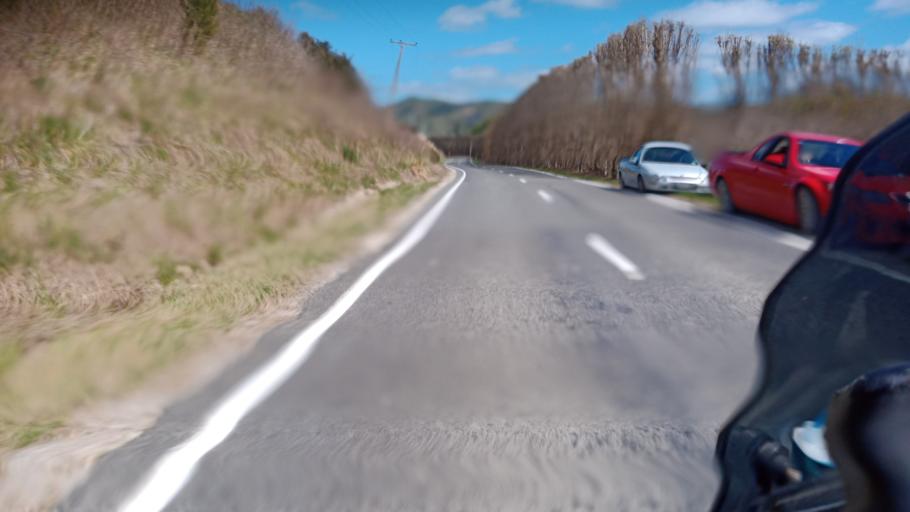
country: NZ
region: Gisborne
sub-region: Gisborne District
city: Gisborne
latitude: -38.6816
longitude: 177.8891
